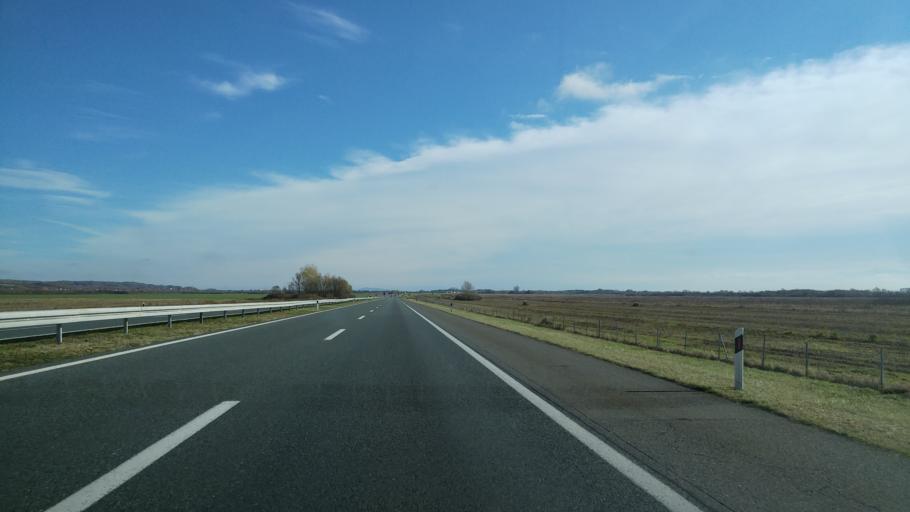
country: HR
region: Brodsko-Posavska
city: Okucani
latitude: 45.2674
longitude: 17.1467
